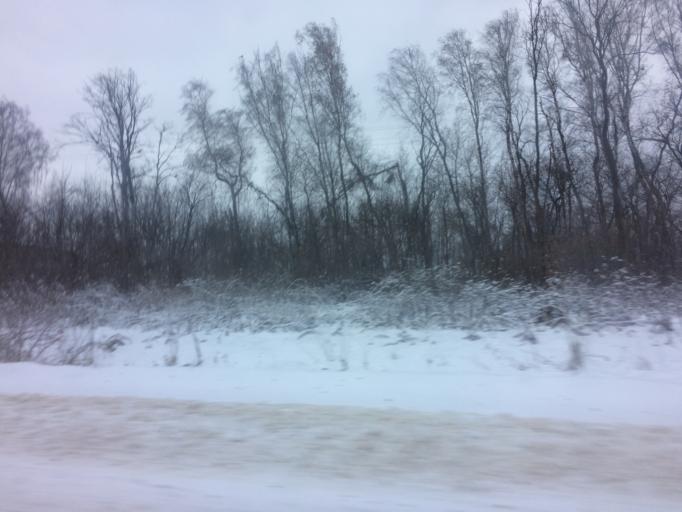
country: RU
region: Tula
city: Tula
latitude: 54.1450
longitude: 37.6515
